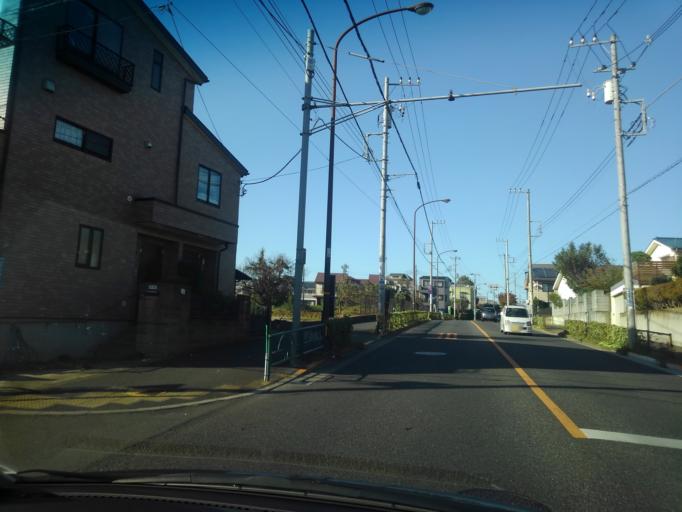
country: JP
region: Tokyo
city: Mitaka-shi
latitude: 35.6788
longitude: 139.5388
